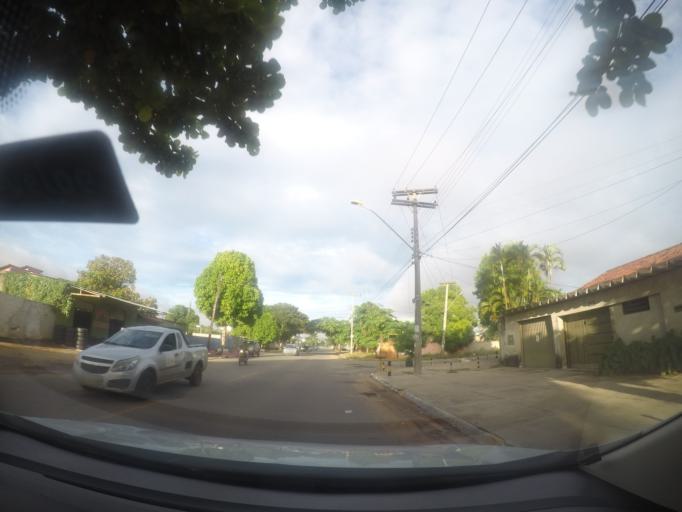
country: BR
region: Goias
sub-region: Goiania
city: Goiania
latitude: -16.6865
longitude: -49.3093
